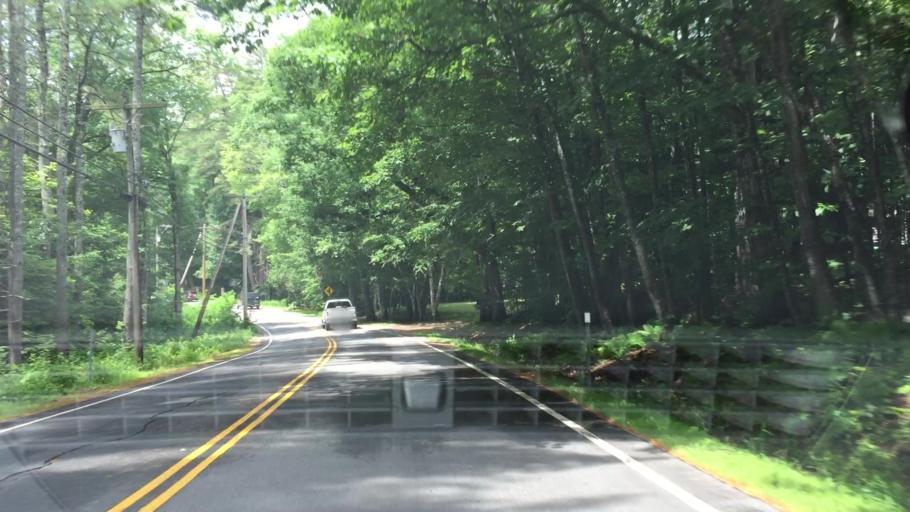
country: US
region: New Hampshire
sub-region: Grafton County
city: Holderness
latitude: 43.7407
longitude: -71.5817
